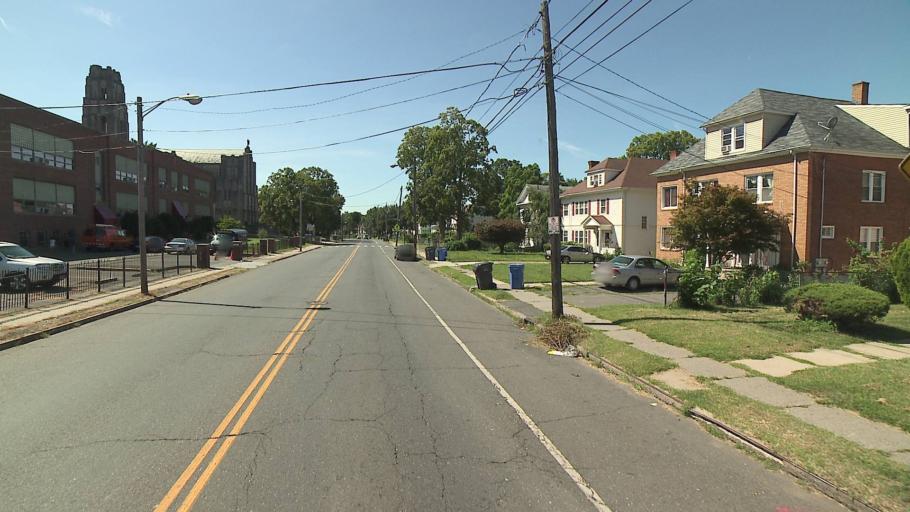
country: US
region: Connecticut
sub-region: Hartford County
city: Blue Hills
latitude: 41.7920
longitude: -72.6979
